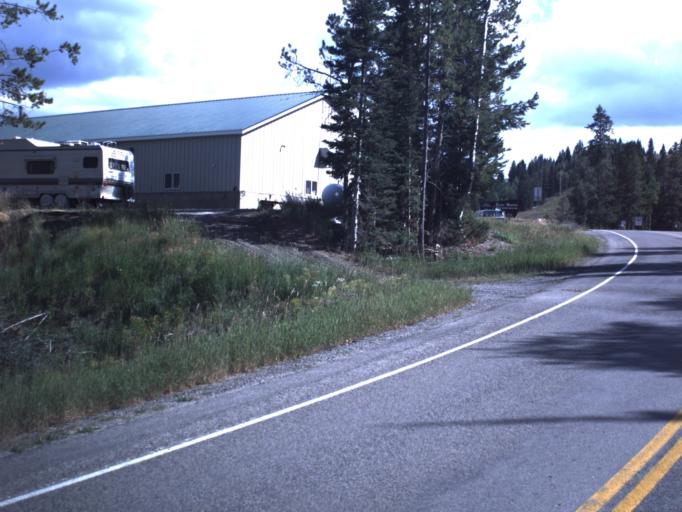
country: US
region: Utah
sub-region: Cache County
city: Richmond
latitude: 41.9706
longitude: -111.5402
